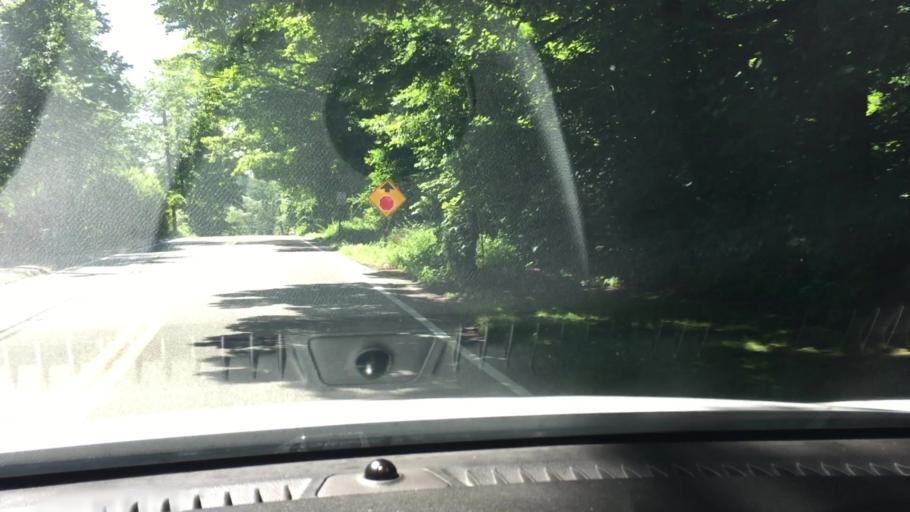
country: US
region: Massachusetts
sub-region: Berkshire County
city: Lenox
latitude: 42.3580
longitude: -73.2596
